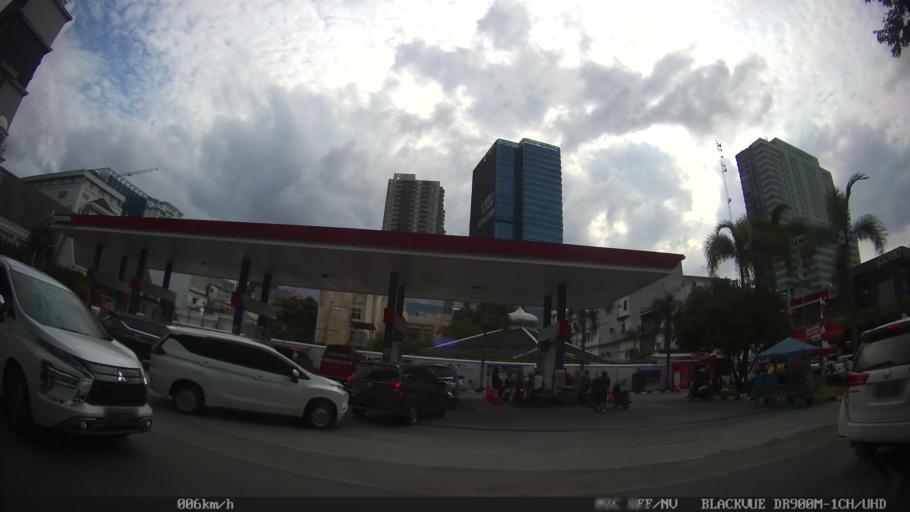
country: ID
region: North Sumatra
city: Medan
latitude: 3.5953
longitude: 98.6772
